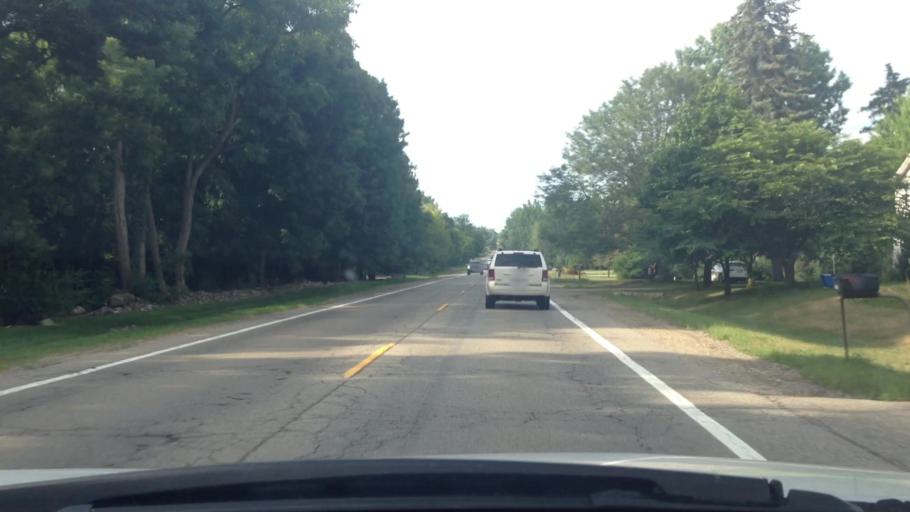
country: US
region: Michigan
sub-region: Oakland County
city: Clarkston
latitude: 42.7402
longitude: -83.3503
